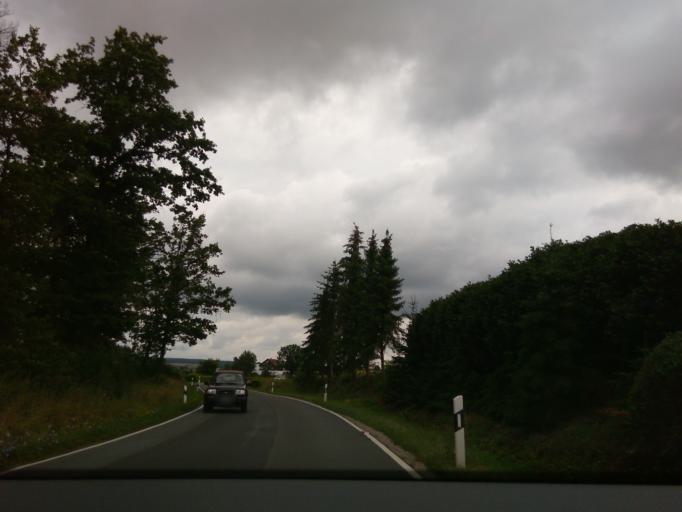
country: DE
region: Bavaria
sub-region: Regierungsbezirk Mittelfranken
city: Hochstadt an der Aisch
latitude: 49.6886
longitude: 10.8043
